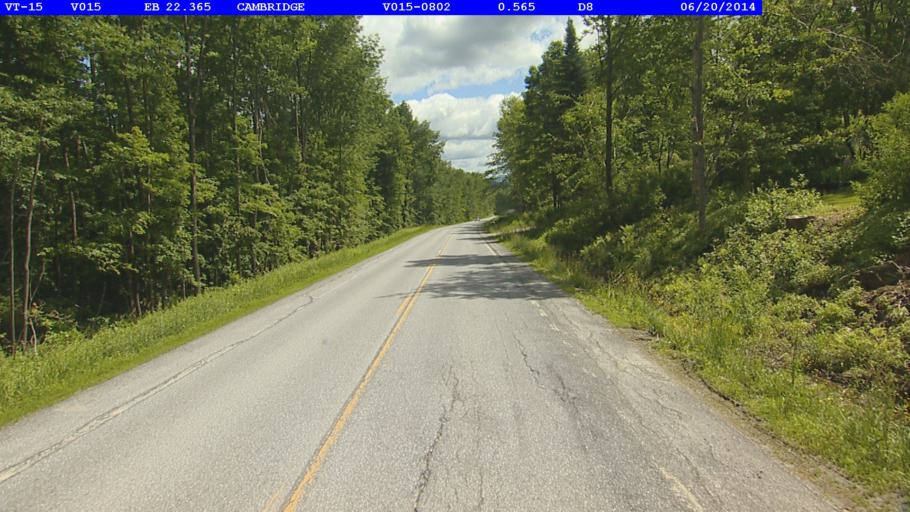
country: US
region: Vermont
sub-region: Chittenden County
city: Jericho
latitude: 44.6372
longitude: -72.9080
